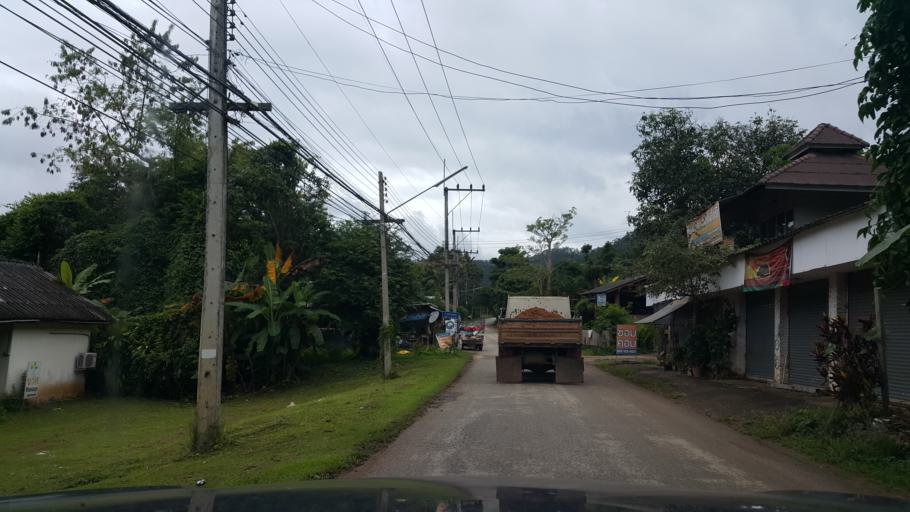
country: TH
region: Chiang Mai
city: Samoeng
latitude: 18.8532
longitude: 98.7324
